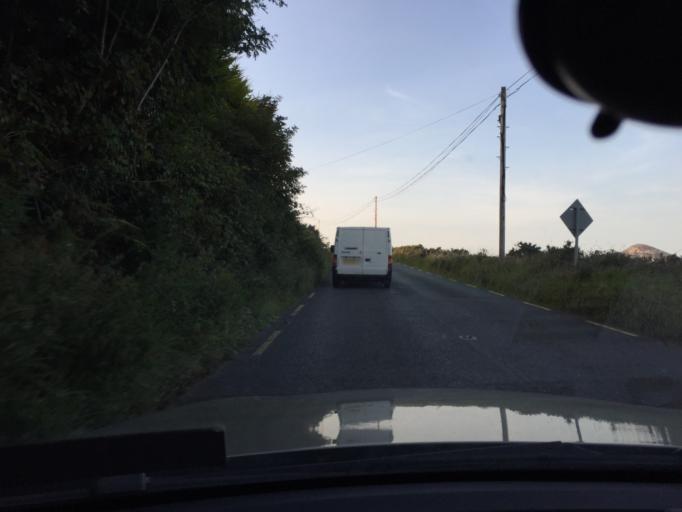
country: IE
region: Leinster
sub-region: Wicklow
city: Kilmacanoge
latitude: 53.1313
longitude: -6.1770
